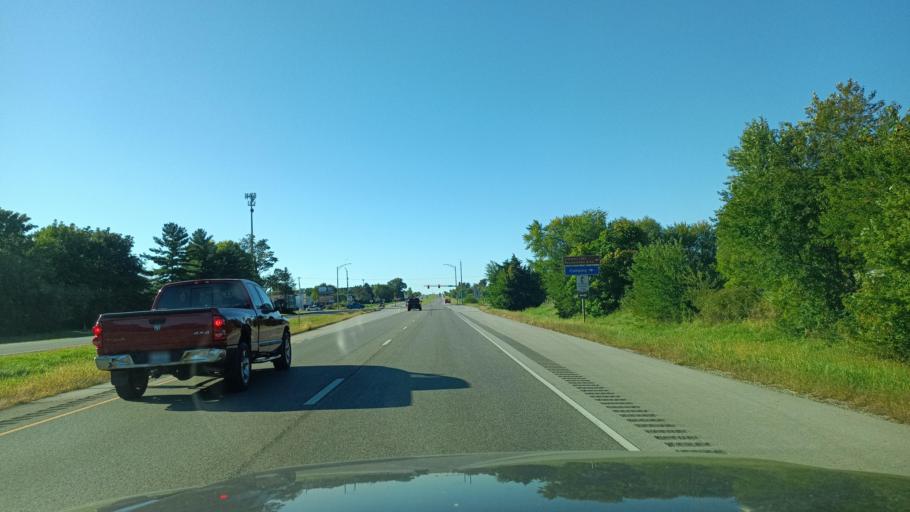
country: US
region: Illinois
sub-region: Warren County
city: Monmouth
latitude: 40.9144
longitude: -90.6633
